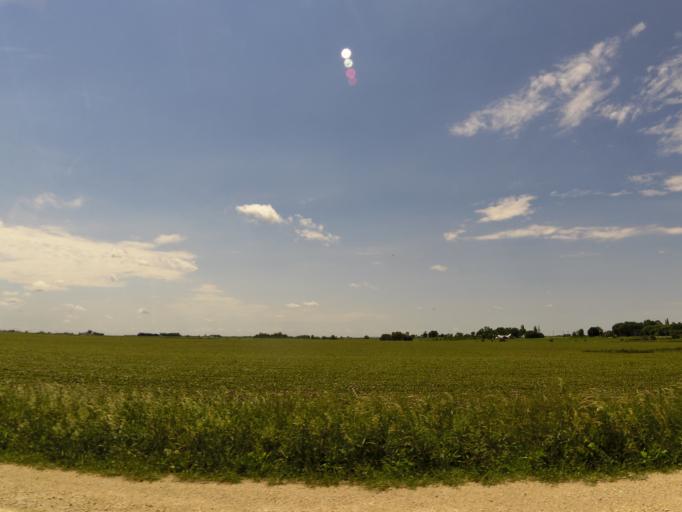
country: US
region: Iowa
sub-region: Buchanan County
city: Fairbank
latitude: 42.7146
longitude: -92.0982
